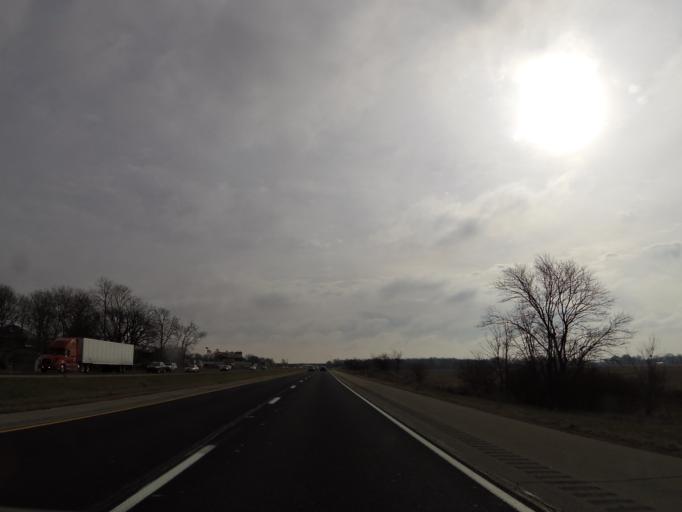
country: US
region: Indiana
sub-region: Hancock County
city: New Palestine
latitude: 39.6674
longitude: -85.9505
